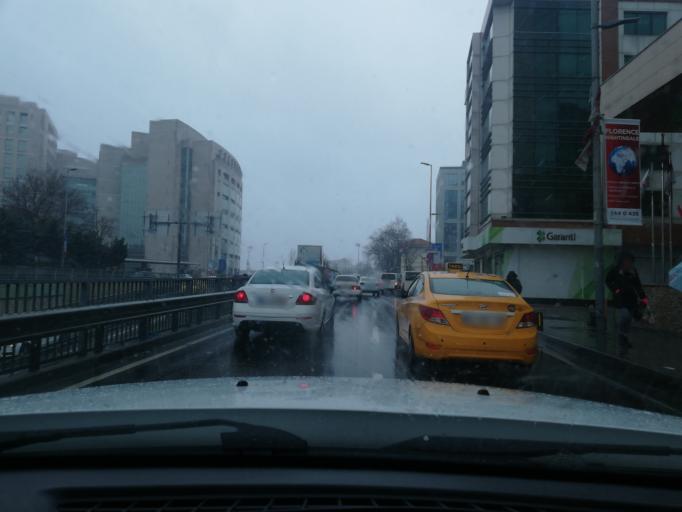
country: TR
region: Istanbul
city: Sisli
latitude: 41.0690
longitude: 28.9830
